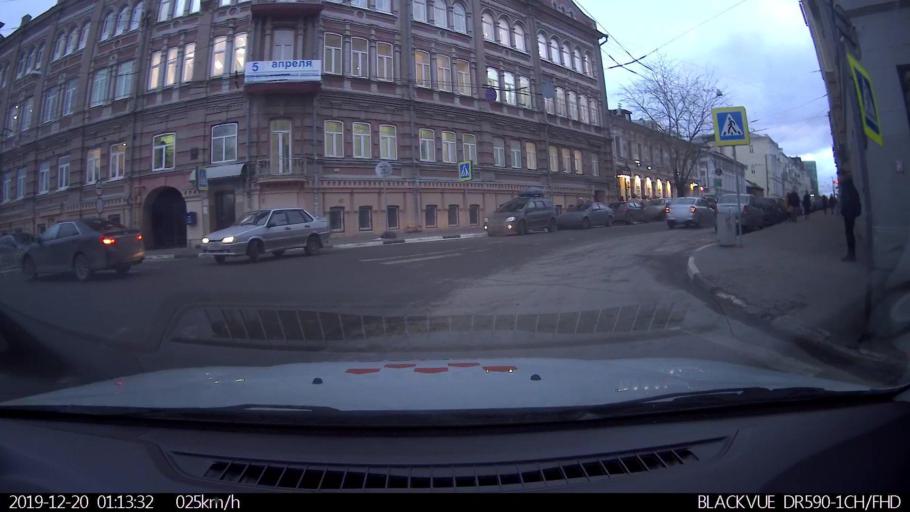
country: RU
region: Nizjnij Novgorod
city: Nizhniy Novgorod
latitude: 56.3265
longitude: 44.0081
